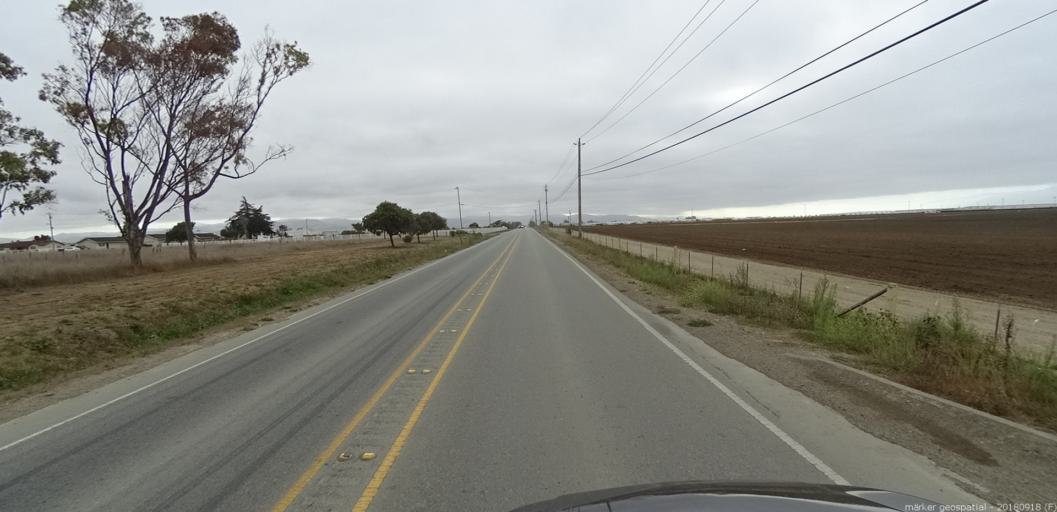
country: US
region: California
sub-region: Monterey County
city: Prunedale
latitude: 36.7442
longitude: -121.6911
